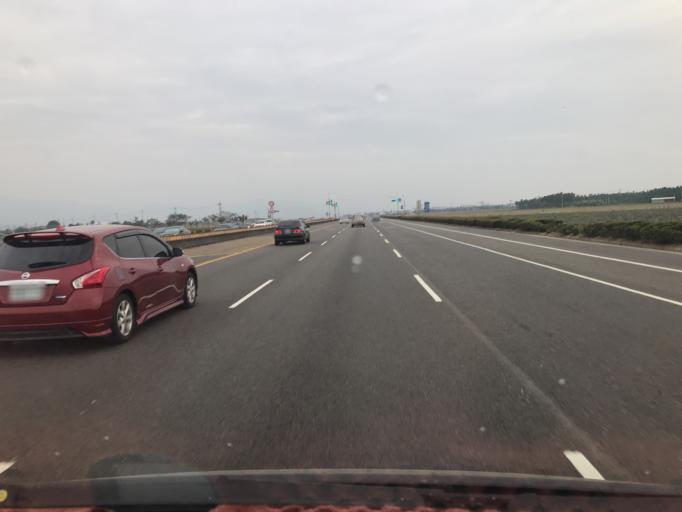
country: TW
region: Taiwan
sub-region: Pingtung
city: Pingtung
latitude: 22.4329
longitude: 120.5717
